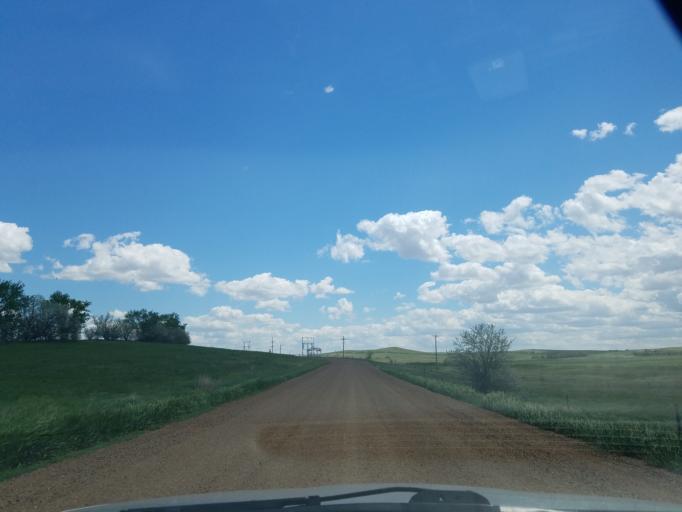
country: US
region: North Dakota
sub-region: Williams County
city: Williston
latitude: 47.8345
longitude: -103.6346
